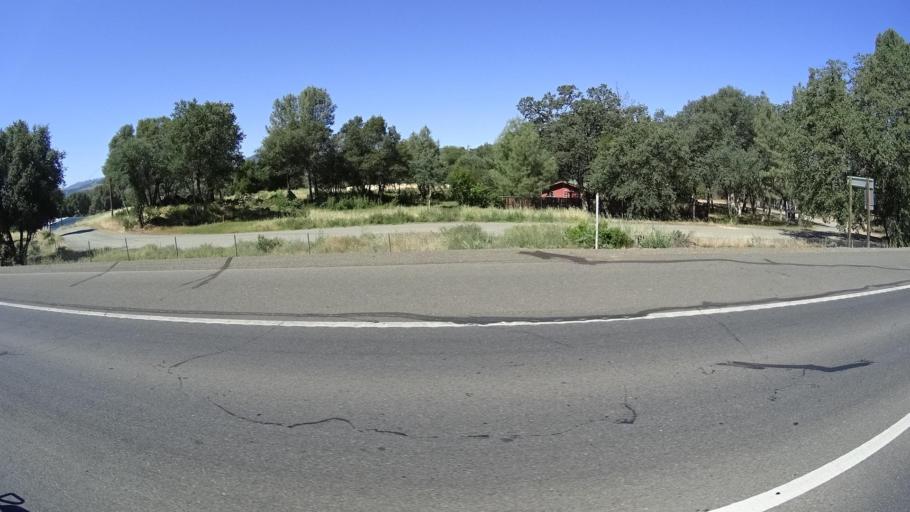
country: US
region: California
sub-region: Lake County
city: Clearlake
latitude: 38.9379
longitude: -122.6230
